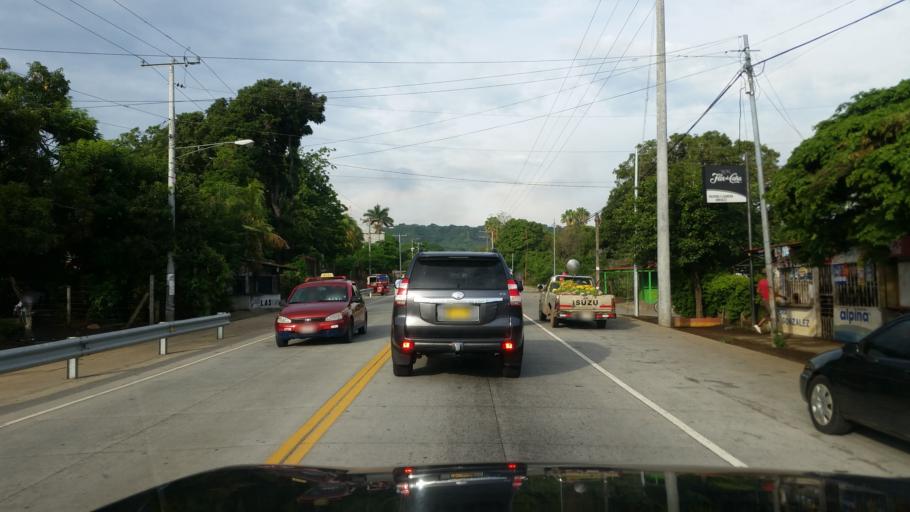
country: NI
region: Managua
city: Ciudad Sandino
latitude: 12.0906
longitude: -86.3551
